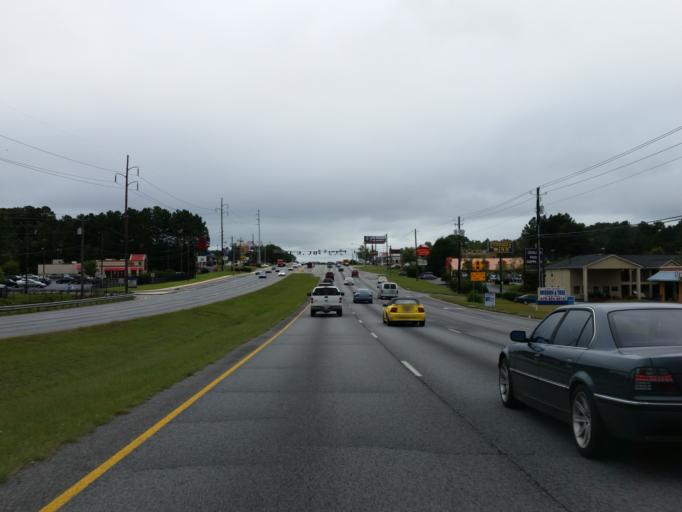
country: US
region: Georgia
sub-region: Clayton County
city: Jonesboro
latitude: 33.5255
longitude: -84.3633
